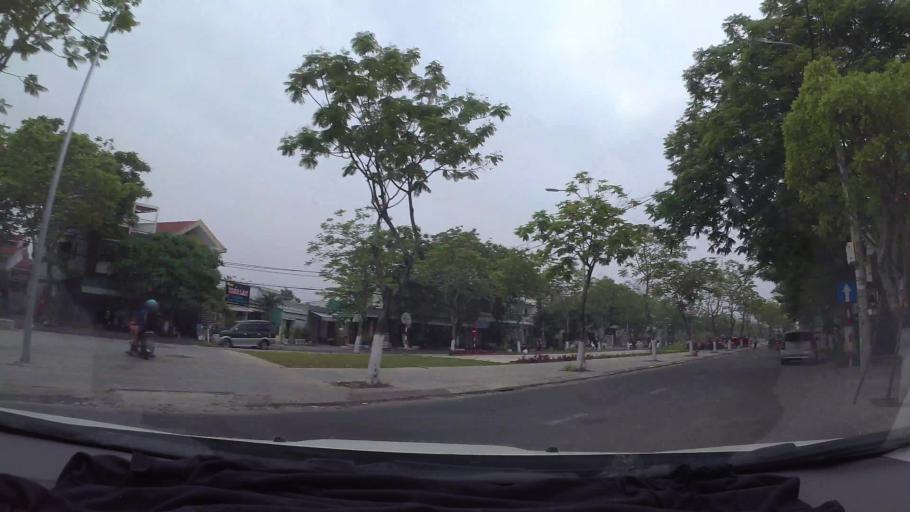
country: VN
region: Da Nang
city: Thanh Khe
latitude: 16.0492
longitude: 108.1790
